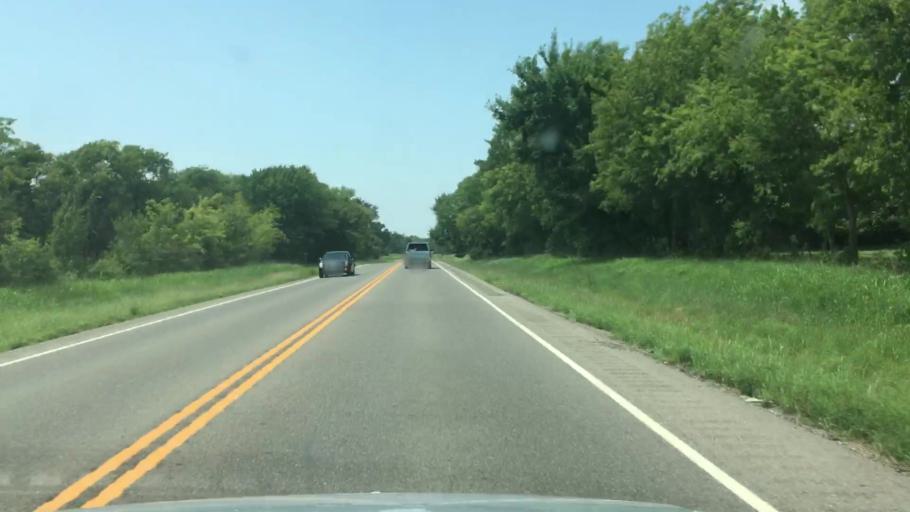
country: US
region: Oklahoma
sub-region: Wagoner County
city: Wagoner
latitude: 35.9387
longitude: -95.3079
